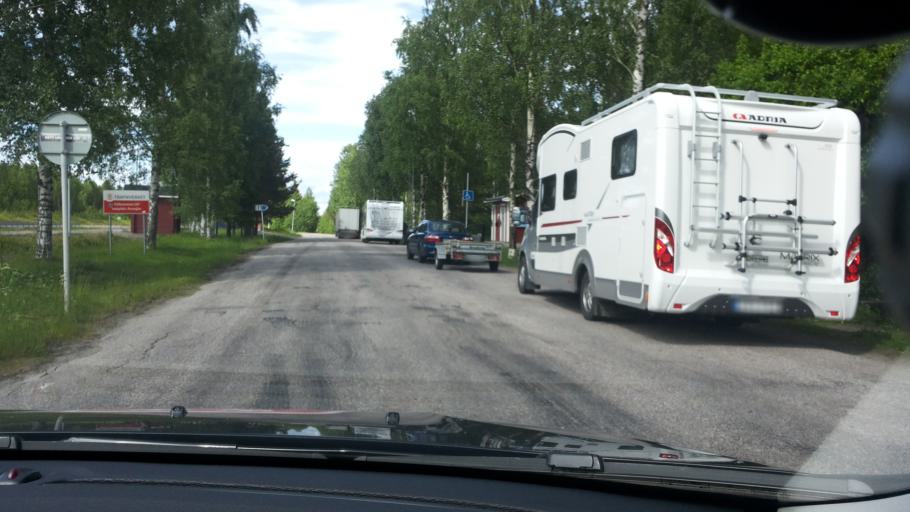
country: SE
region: Vaesternorrland
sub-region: Sundsvalls Kommun
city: Njurundabommen
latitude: 62.1684
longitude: 17.3562
